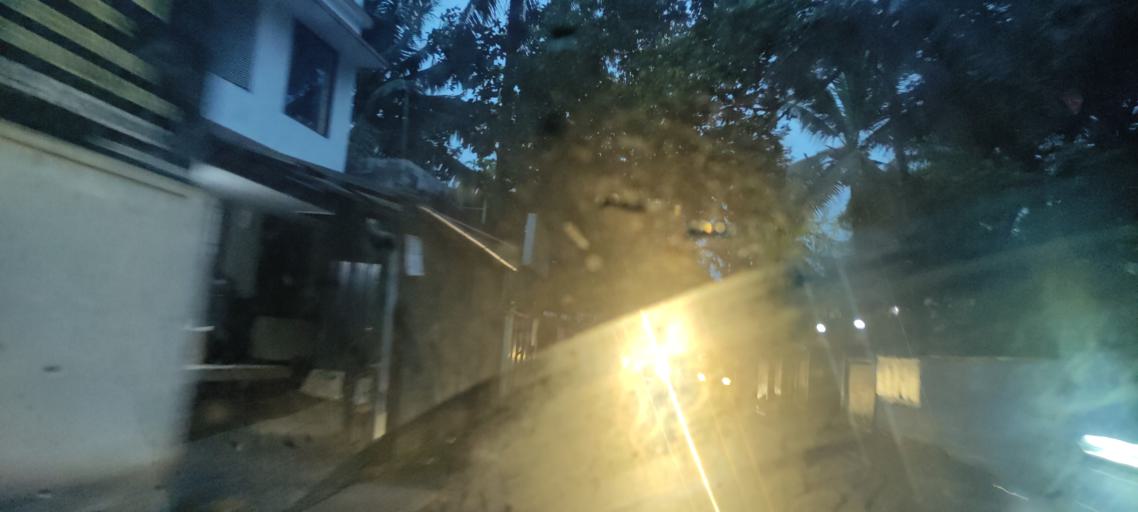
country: IN
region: Kerala
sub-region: Ernakulam
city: Cochin
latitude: 9.9158
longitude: 76.2912
